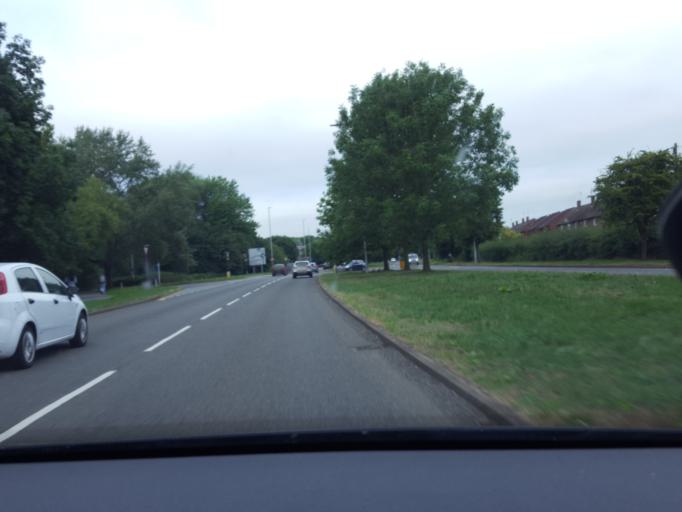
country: GB
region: England
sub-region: Leicestershire
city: Hathern
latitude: 52.7642
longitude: -1.2413
